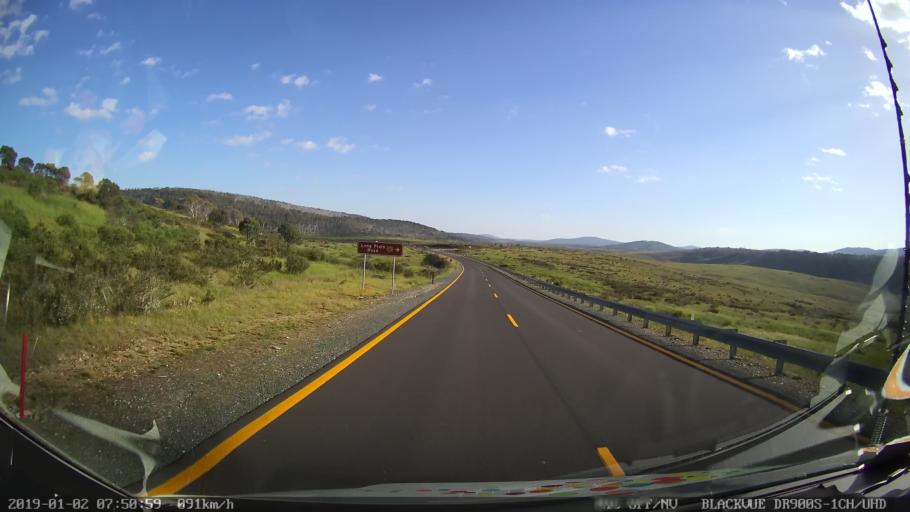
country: AU
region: New South Wales
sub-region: Tumut Shire
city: Tumut
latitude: -35.7238
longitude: 148.5303
